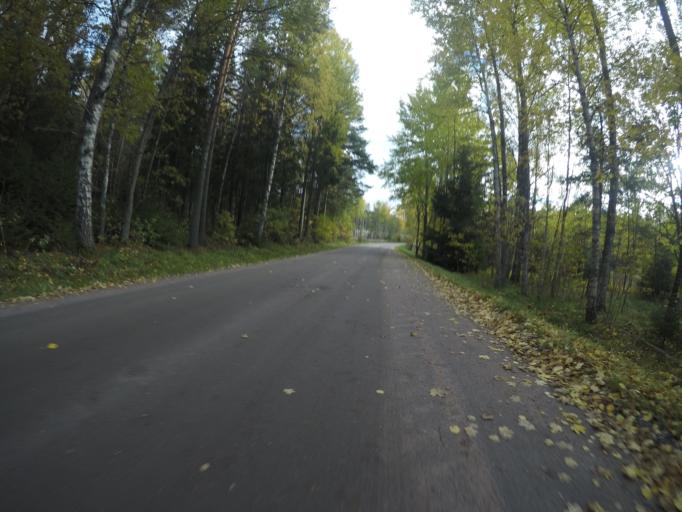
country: SE
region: Vaestmanland
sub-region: Arboga Kommun
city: Tyringe
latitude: 59.3793
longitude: 15.9485
